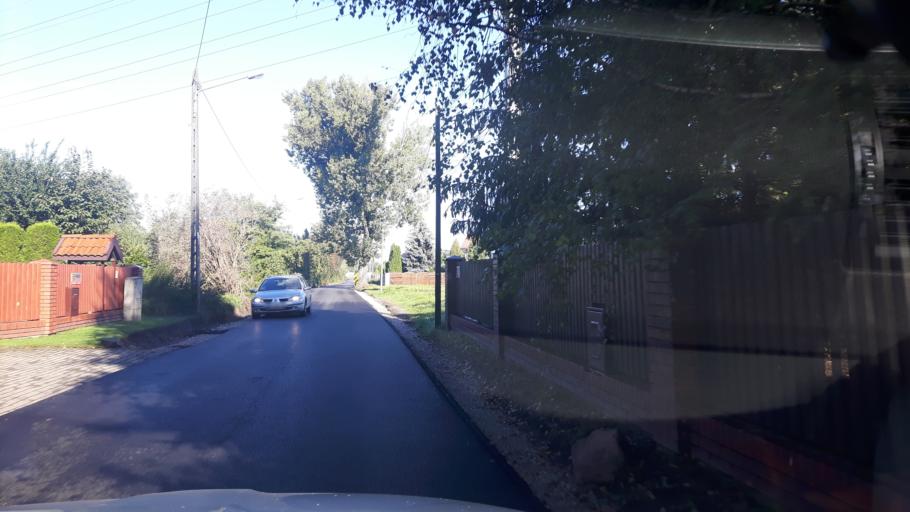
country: PL
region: Masovian Voivodeship
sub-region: Powiat legionowski
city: Stanislawow Pierwszy
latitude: 52.3603
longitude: 21.0301
